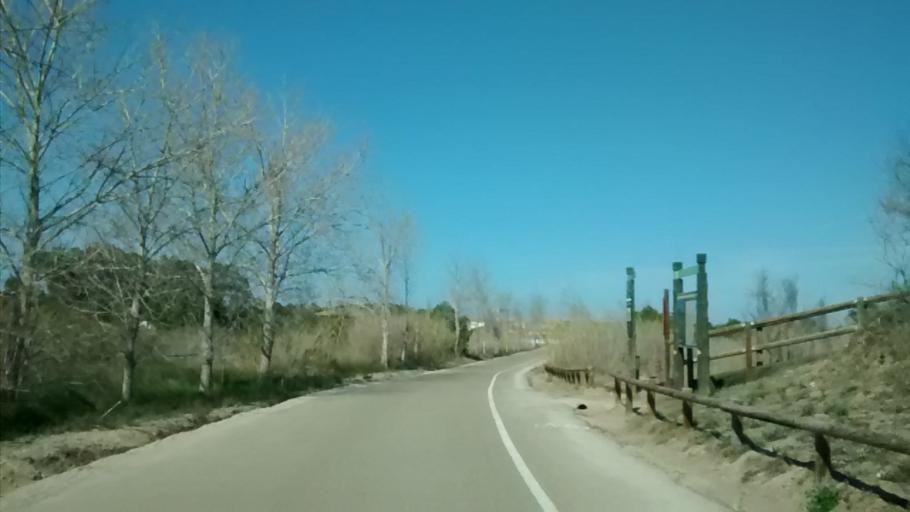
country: ES
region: Catalonia
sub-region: Provincia de Tarragona
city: Deltebre
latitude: 40.7182
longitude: 0.8473
